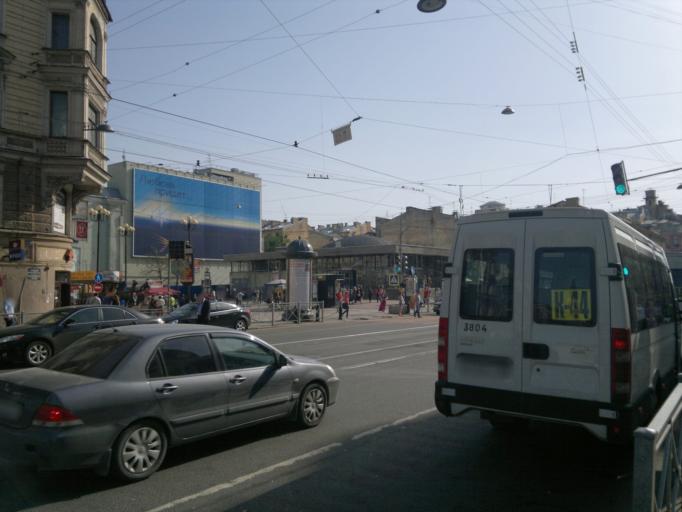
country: RU
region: St.-Petersburg
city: Vasyl'evsky Ostrov
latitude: 59.9433
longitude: 30.2789
